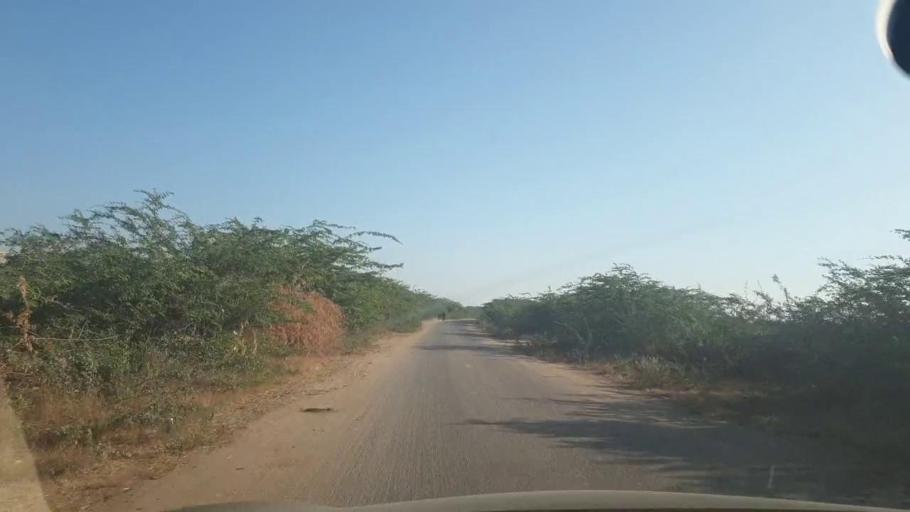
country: PK
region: Sindh
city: Malir Cantonment
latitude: 25.1125
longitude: 67.2685
